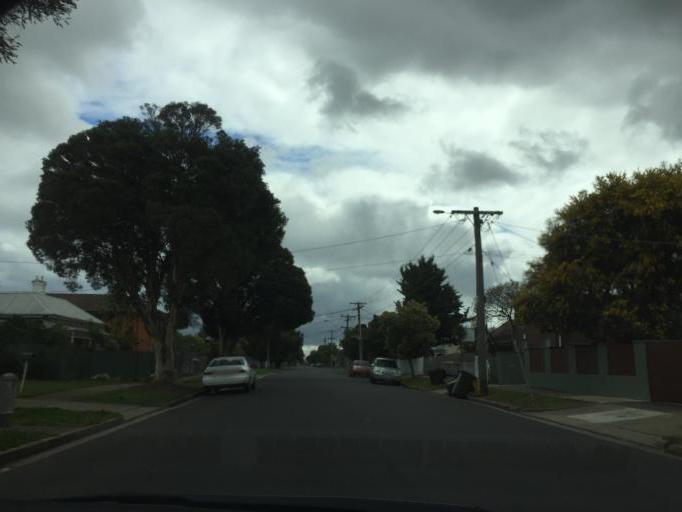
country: AU
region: Victoria
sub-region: Brimbank
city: Sunshine West
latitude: -37.7847
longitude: 144.8220
